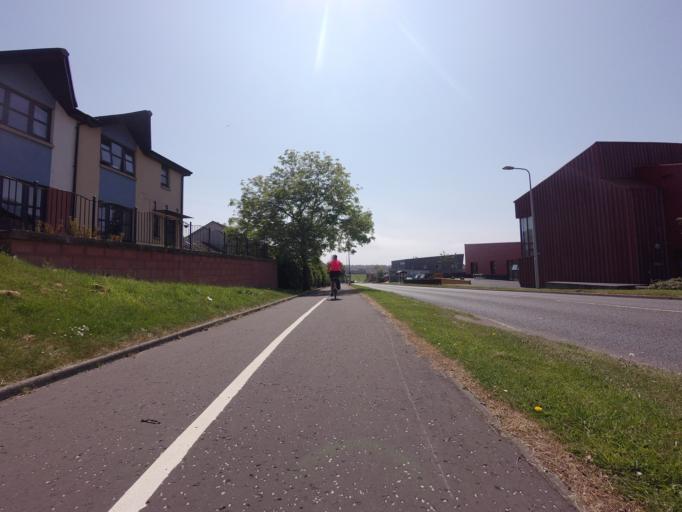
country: GB
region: Scotland
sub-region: Fife
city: Townhill
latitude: 56.0665
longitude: -3.4159
